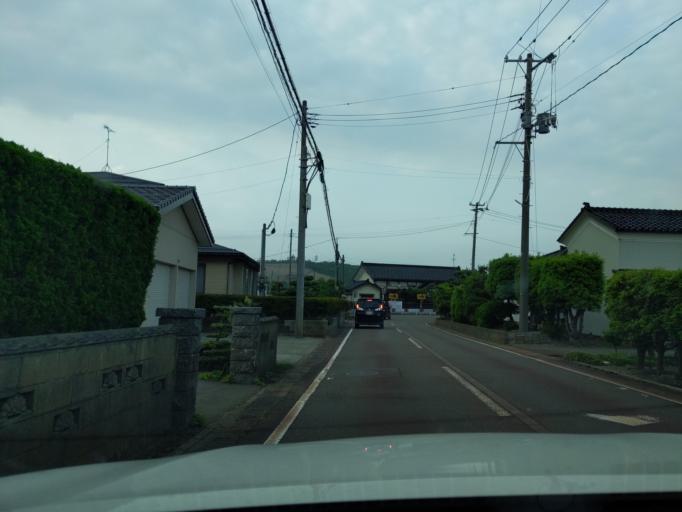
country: JP
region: Niigata
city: Kashiwazaki
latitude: 37.3894
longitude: 138.5857
